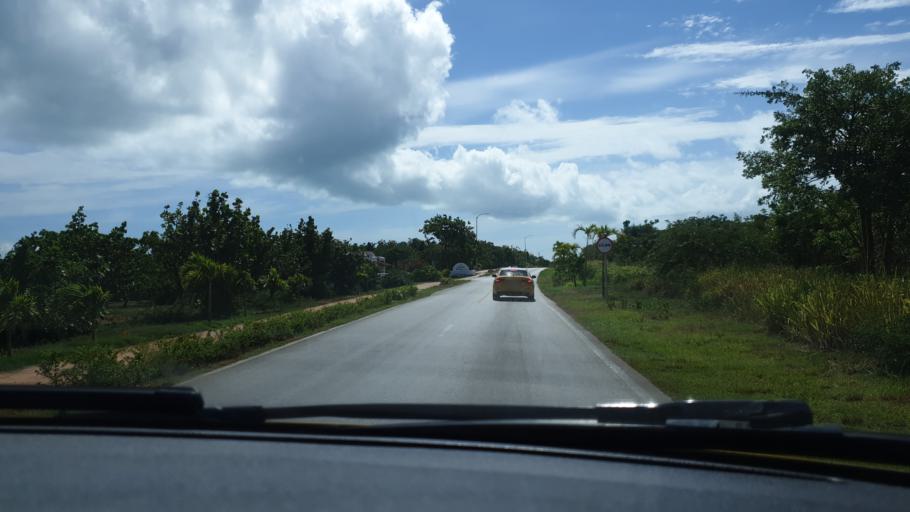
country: CU
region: Sancti Spiritus
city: Yaguajay
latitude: 22.6558
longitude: -79.0319
